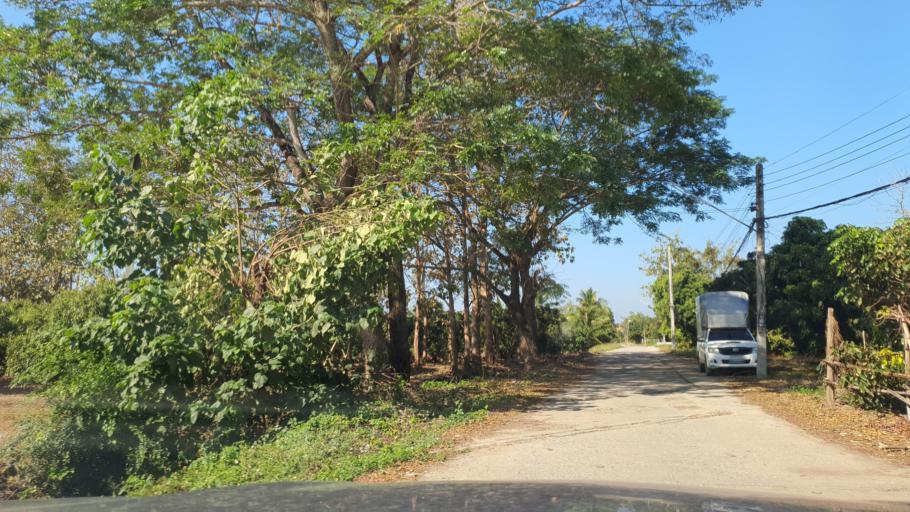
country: TH
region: Chiang Mai
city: Saraphi
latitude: 18.7019
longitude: 99.0761
